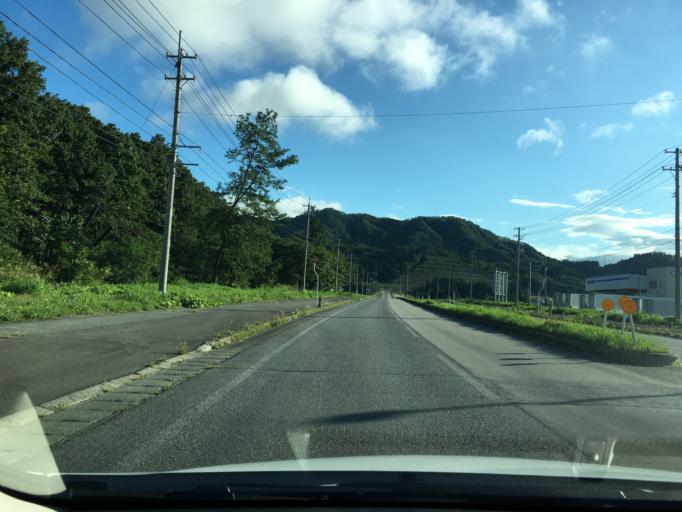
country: JP
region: Yamagata
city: Yonezawa
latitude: 37.9006
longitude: 140.1663
